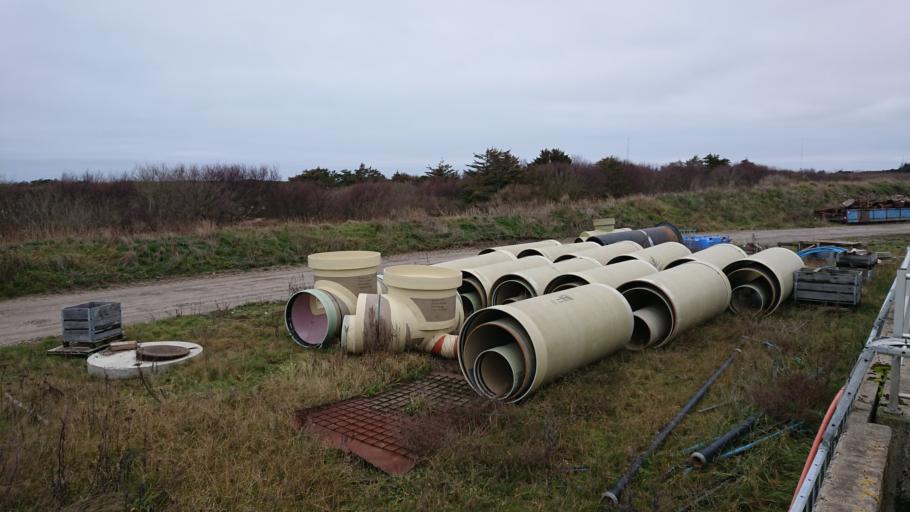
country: DK
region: North Denmark
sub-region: Frederikshavn Kommune
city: Skagen
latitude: 57.7391
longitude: 10.5678
